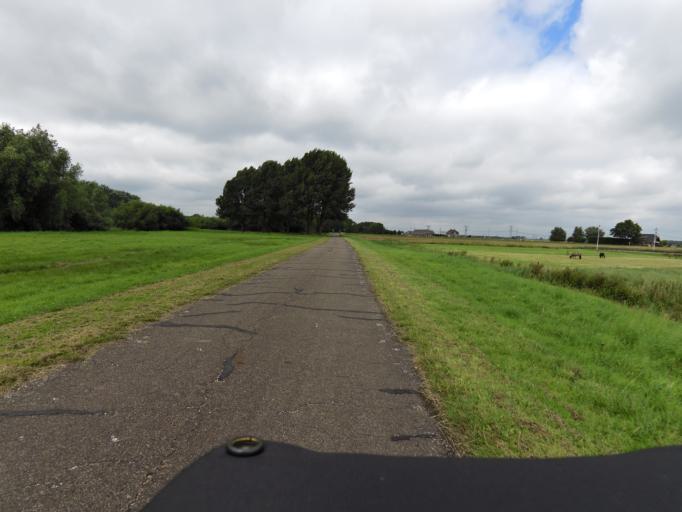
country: NL
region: South Holland
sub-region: Gemeente Spijkenisse
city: Spijkenisse
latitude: 51.8267
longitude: 4.2663
